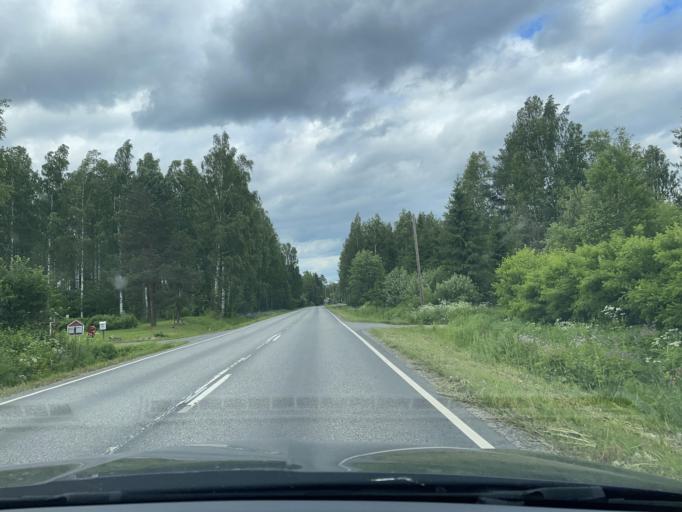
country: FI
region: Central Finland
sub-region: Jyvaeskylae
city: Petaejaevesi
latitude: 62.2442
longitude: 25.1672
